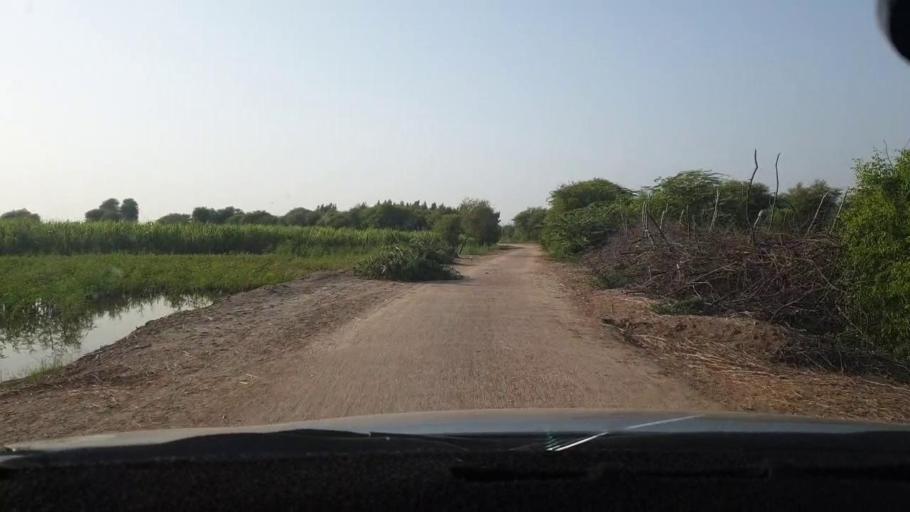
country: PK
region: Sindh
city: Pithoro
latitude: 25.6622
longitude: 69.4492
